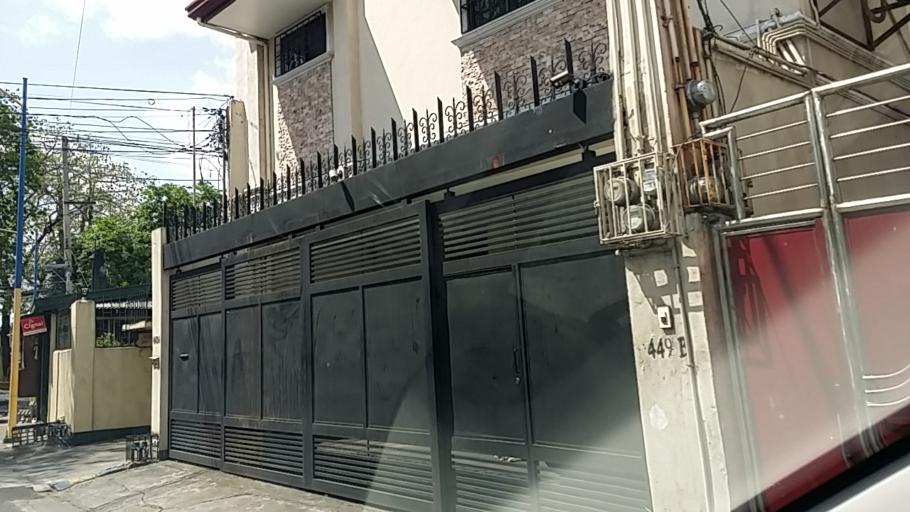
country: PH
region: Metro Manila
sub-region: Mandaluyong
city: Mandaluyong City
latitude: 14.5761
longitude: 121.0458
